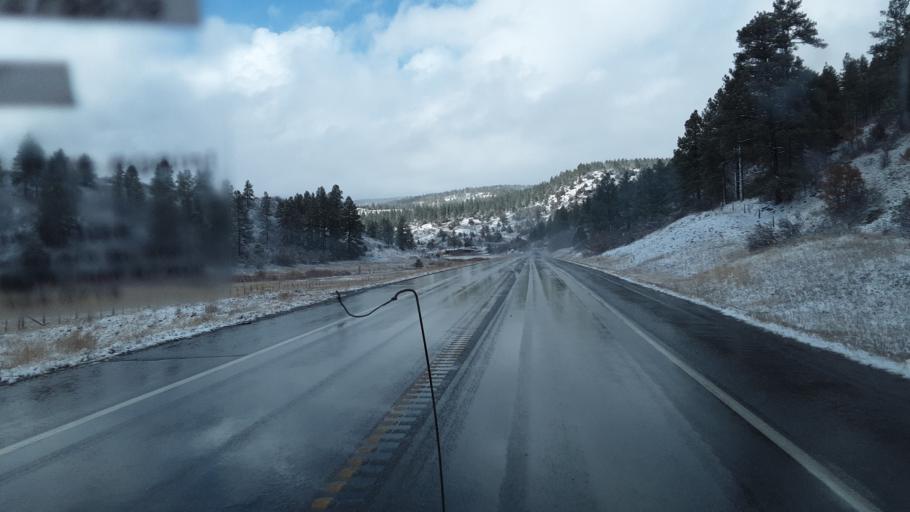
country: US
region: Colorado
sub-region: Archuleta County
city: Pagosa Springs
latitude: 37.2326
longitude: -107.1263
